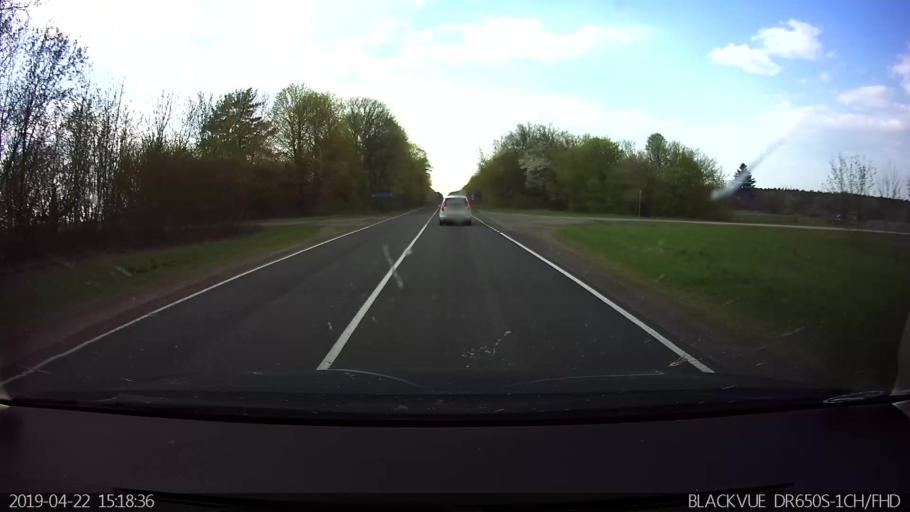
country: BY
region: Brest
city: Vysokaye
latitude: 52.3257
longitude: 23.5509
